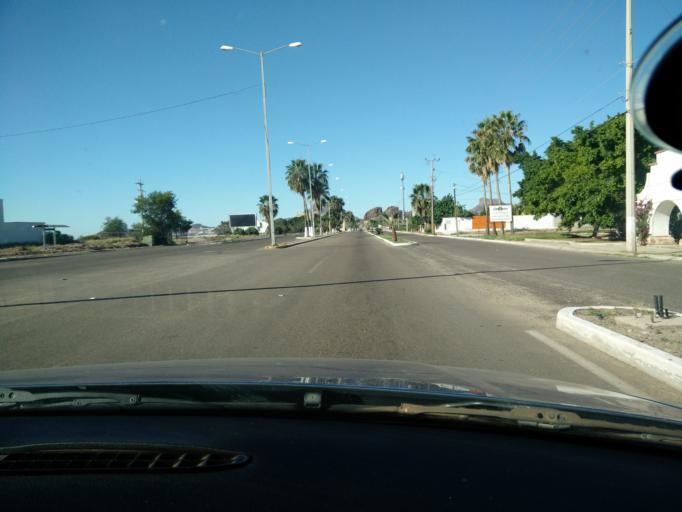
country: MX
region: Sonora
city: Heroica Guaymas
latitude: 27.9659
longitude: -111.0150
